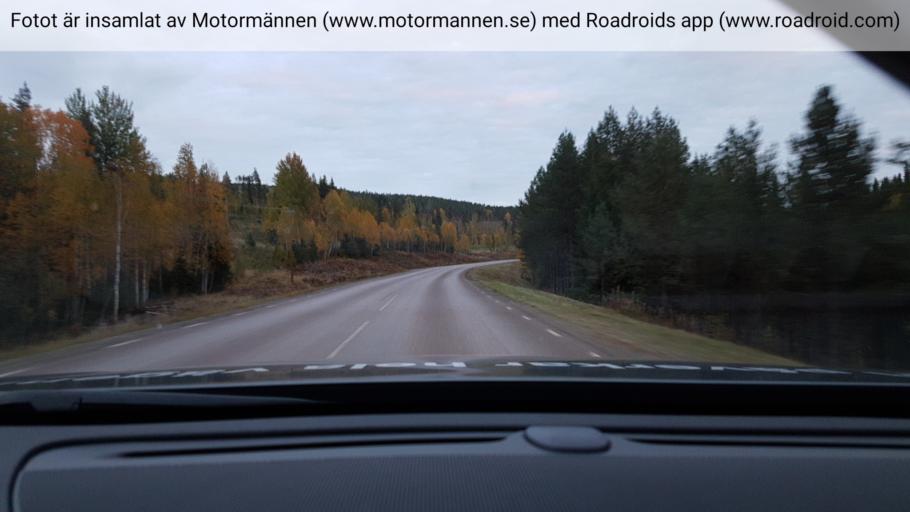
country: SE
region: Norrbotten
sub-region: Alvsbyns Kommun
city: AElvsbyn
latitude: 65.8676
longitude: 20.3972
